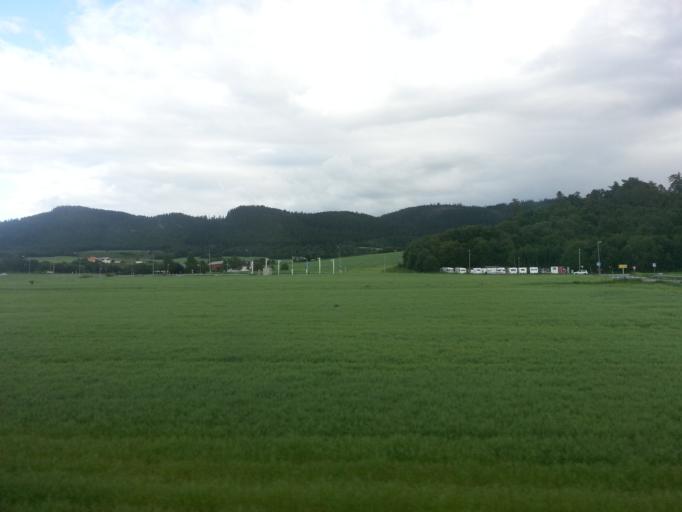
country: NO
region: Sor-Trondelag
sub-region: Malvik
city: Malvik
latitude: 63.4313
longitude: 10.5631
